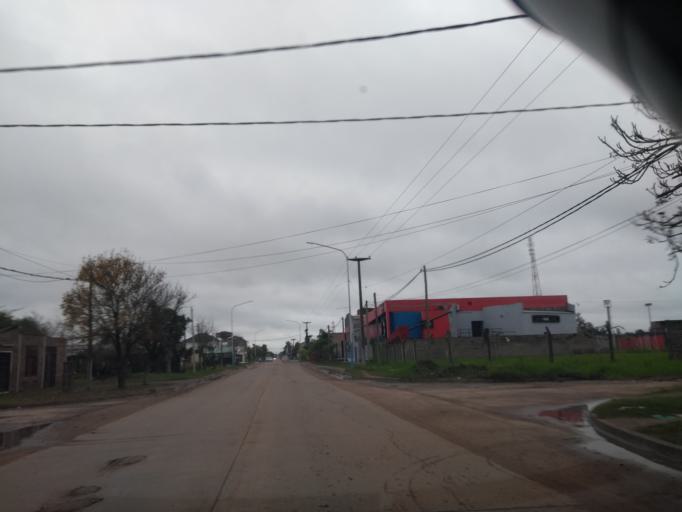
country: AR
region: Chaco
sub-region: Departamento de Quitilipi
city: Quitilipi
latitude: -26.8782
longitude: -60.2204
